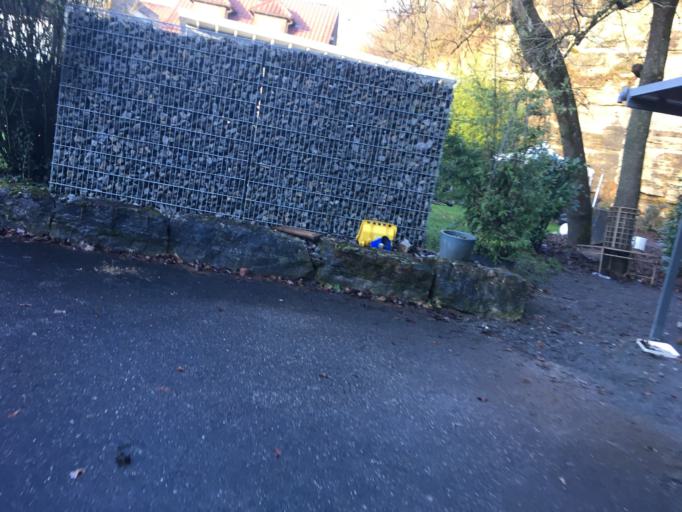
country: DE
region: Baden-Wuerttemberg
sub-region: Regierungsbezirk Stuttgart
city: Talheim
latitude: 49.0779
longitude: 9.1999
